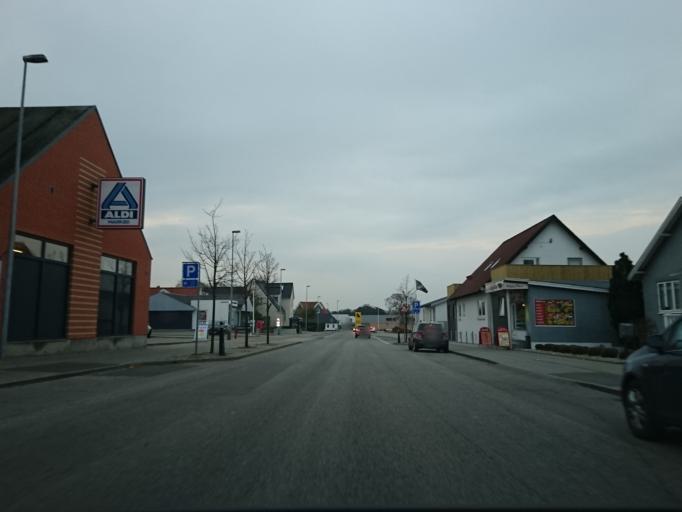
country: DK
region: North Denmark
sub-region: Alborg Kommune
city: Aalborg
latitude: 57.0085
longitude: 9.9265
